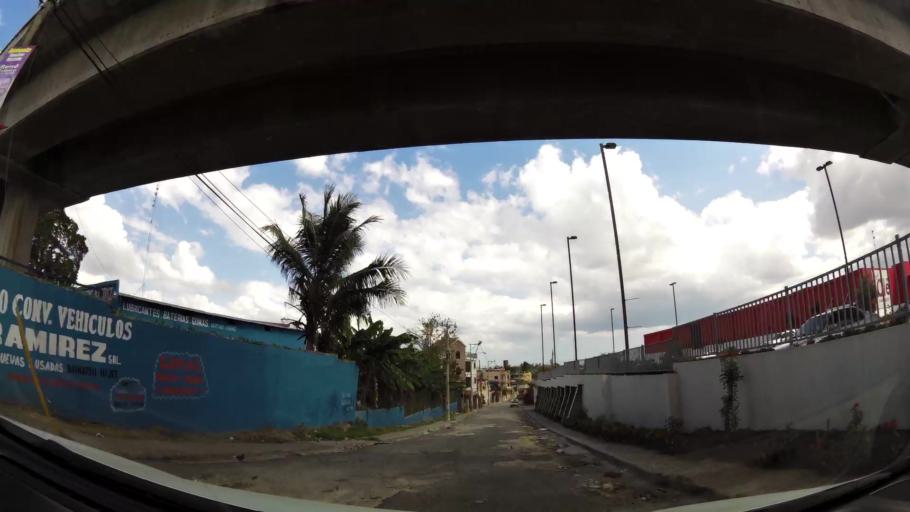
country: DO
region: Nacional
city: Ensanche Luperon
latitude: 18.5427
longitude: -69.9035
